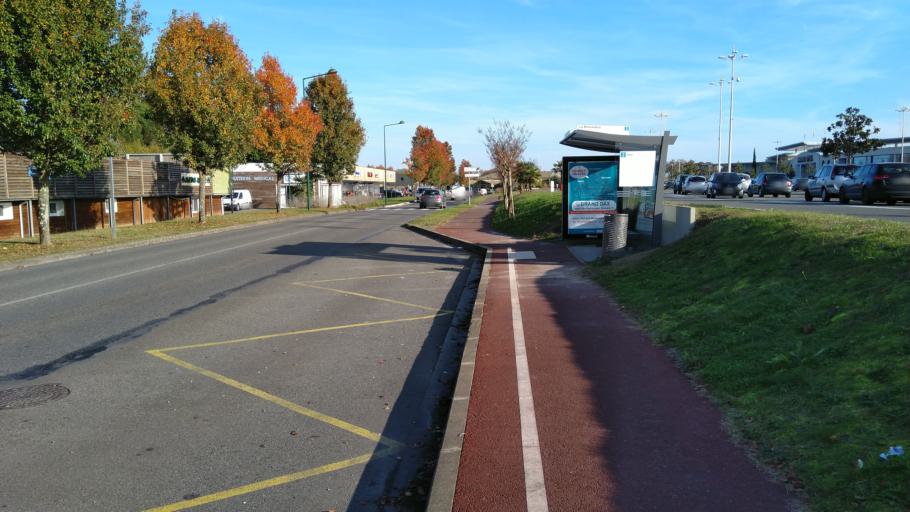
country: FR
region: Aquitaine
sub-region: Departement des Landes
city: Saint-Paul-les-Dax
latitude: 43.7323
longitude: -1.0429
